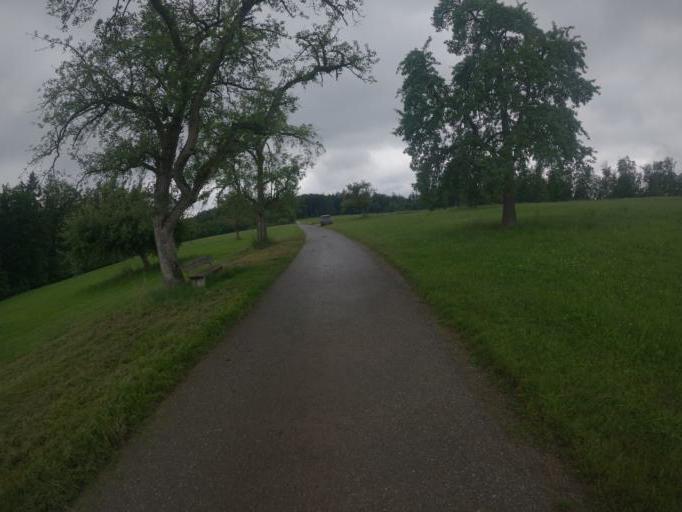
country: DE
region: Baden-Wuerttemberg
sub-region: Regierungsbezirk Stuttgart
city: Schorndorf
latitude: 48.7730
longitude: 9.5417
